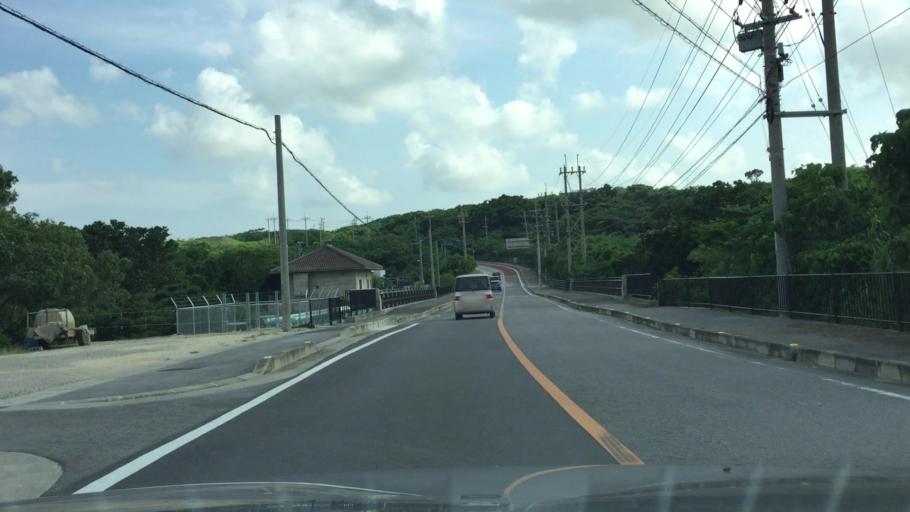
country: JP
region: Okinawa
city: Ishigaki
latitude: 24.4334
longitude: 124.2483
